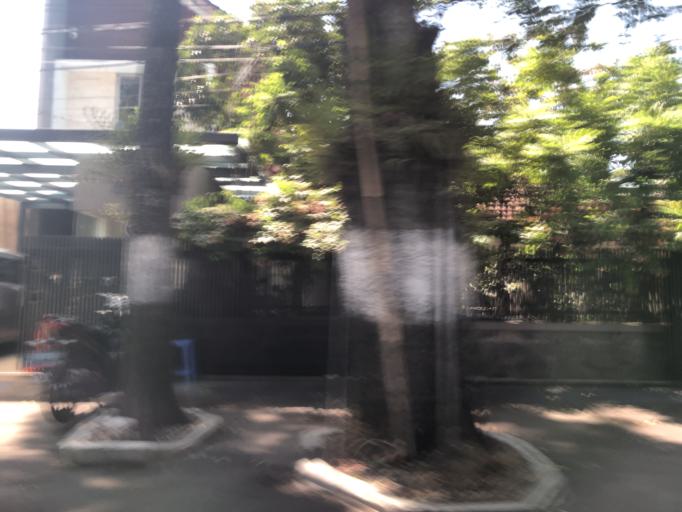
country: ID
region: West Java
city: Bandung
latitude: -6.9118
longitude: 107.6296
